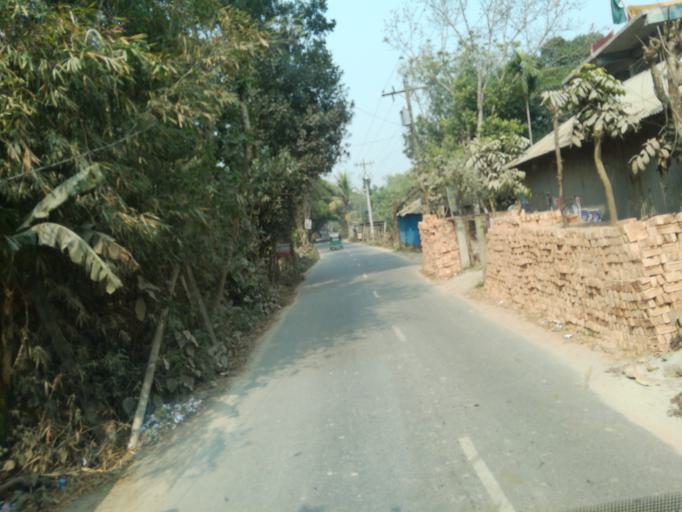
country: BD
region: Dhaka
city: Nagarpur
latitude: 23.9984
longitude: 89.8466
